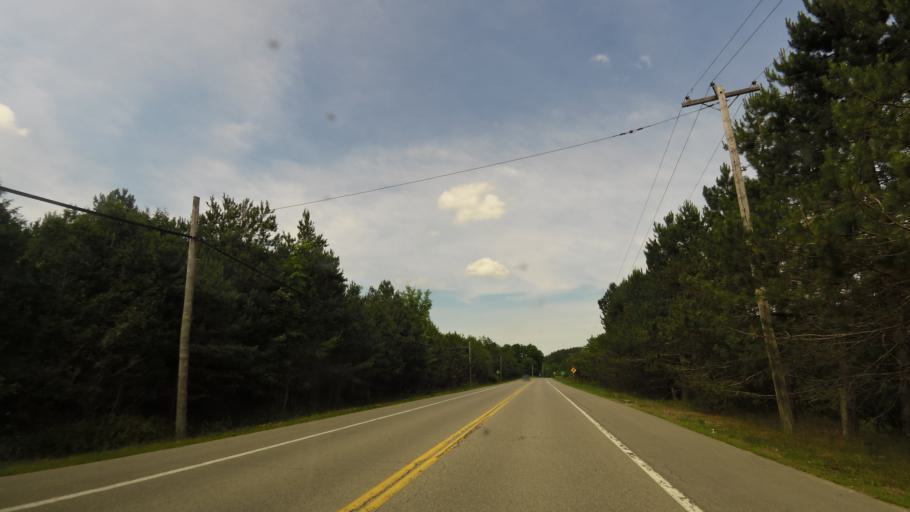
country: CA
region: Ontario
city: Orangeville
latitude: 43.9800
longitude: -80.0489
